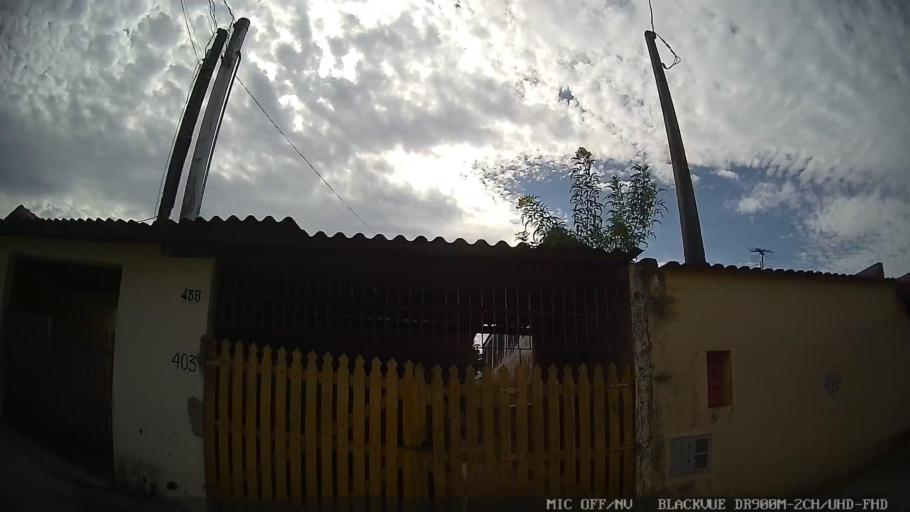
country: BR
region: Sao Paulo
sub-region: Itanhaem
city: Itanhaem
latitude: -24.1604
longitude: -46.7604
